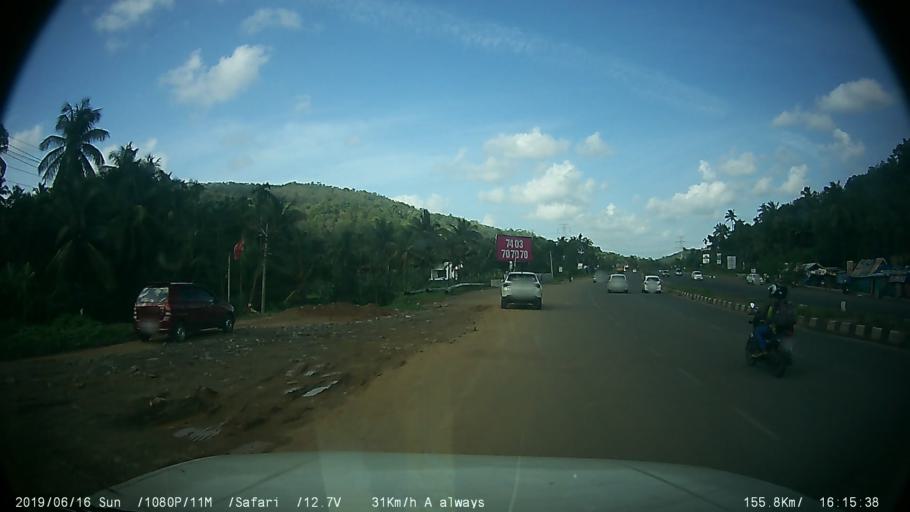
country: IN
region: Kerala
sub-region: Thrissur District
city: Chelakara
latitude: 10.5759
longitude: 76.3938
